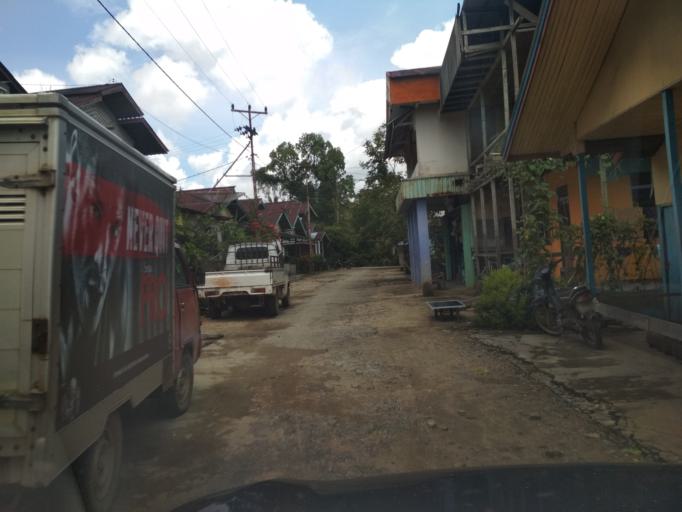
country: ID
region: West Kalimantan
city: Bengkayang
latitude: 0.7519
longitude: 110.1020
